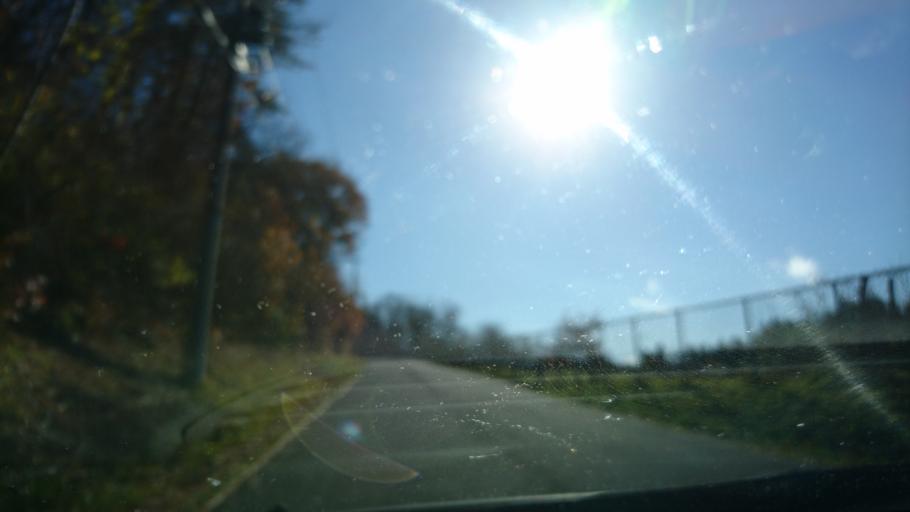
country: JP
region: Iwate
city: Ichinoseki
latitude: 38.9980
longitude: 141.0911
